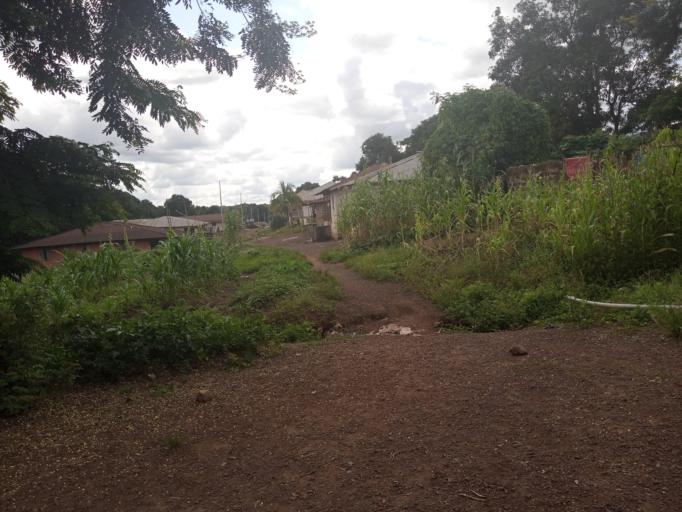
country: SL
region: Northern Province
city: Kamakwie
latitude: 9.4951
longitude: -12.2402
